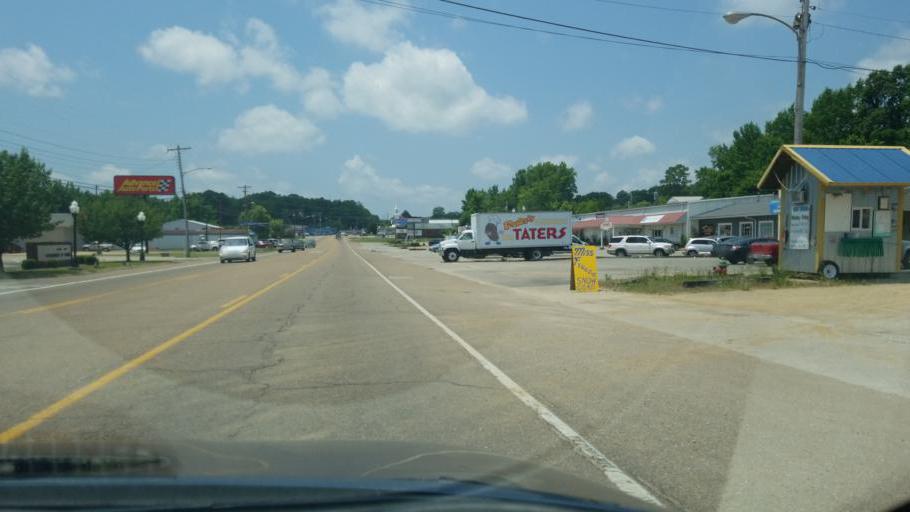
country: US
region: Tennessee
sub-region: Carroll County
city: Huntingdon
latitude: 36.0059
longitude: -88.4096
